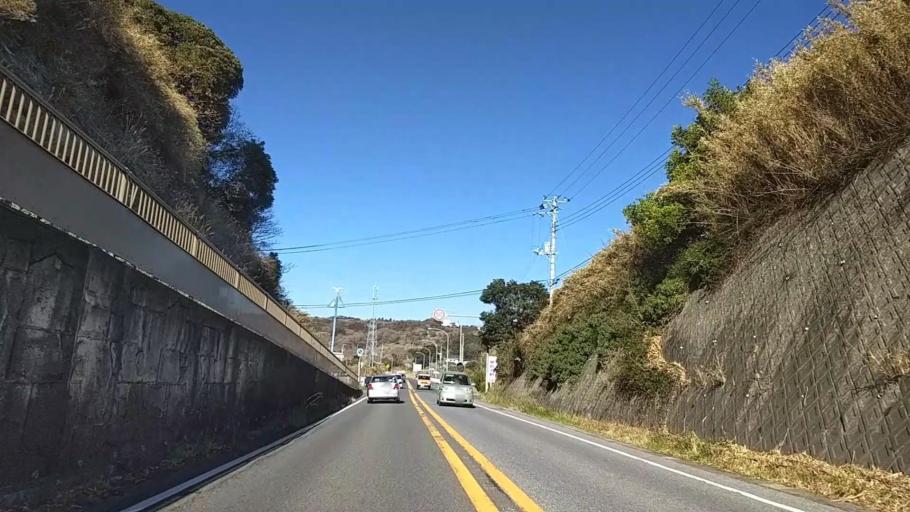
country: JP
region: Chiba
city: Kawaguchi
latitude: 35.0829
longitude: 140.0953
